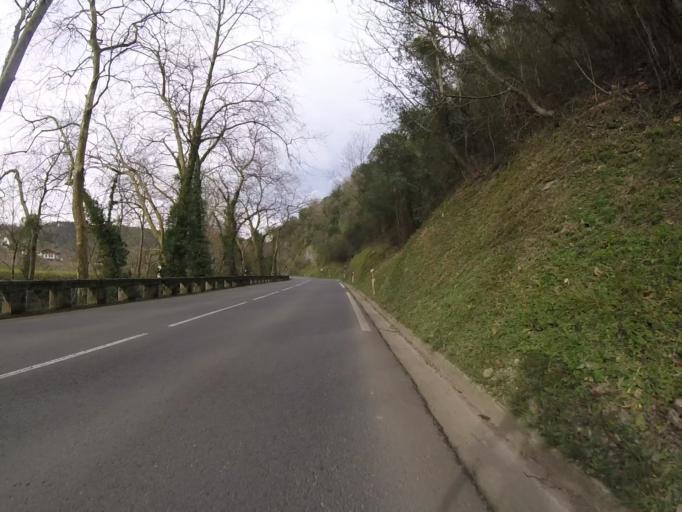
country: ES
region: Basque Country
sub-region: Provincia de Guipuzcoa
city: Aizarnazabal
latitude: 43.2587
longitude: -2.2322
